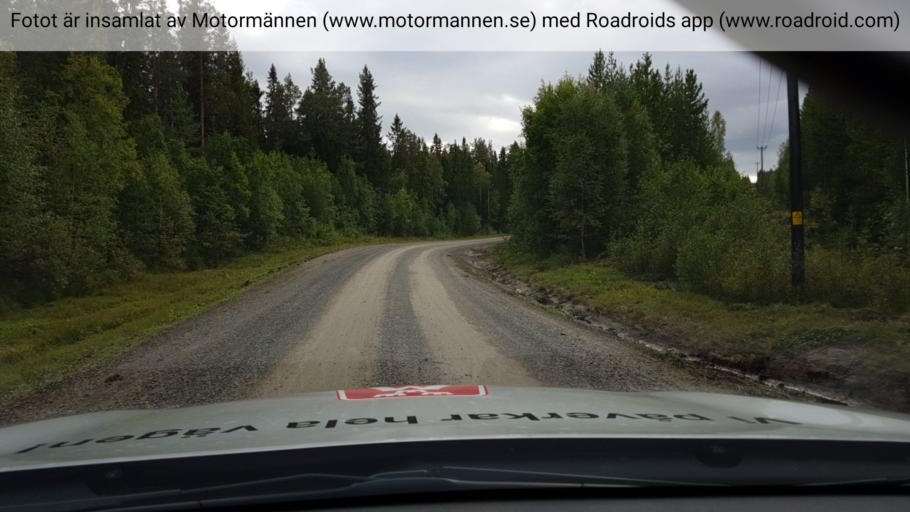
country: SE
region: Jaemtland
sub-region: Ragunda Kommun
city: Hammarstrand
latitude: 62.9241
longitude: 16.1229
